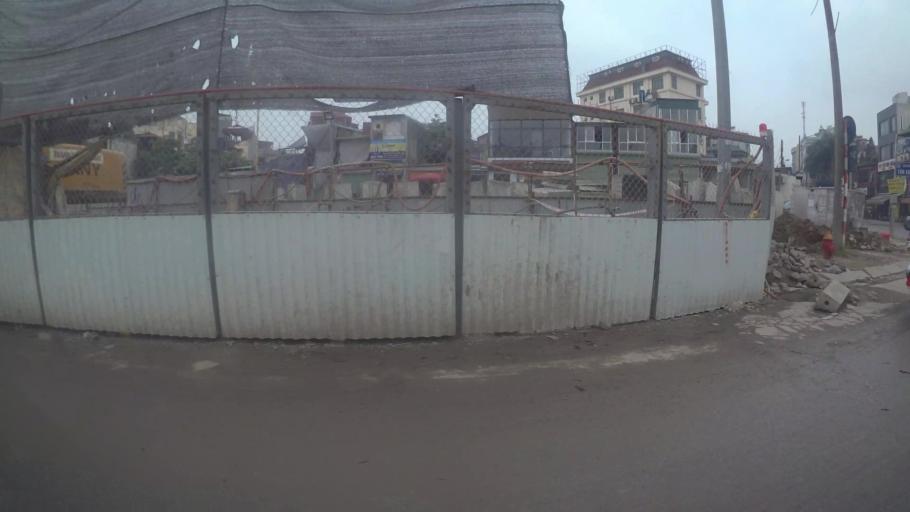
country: VN
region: Ha Noi
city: Tay Ho
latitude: 21.0778
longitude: 105.7869
